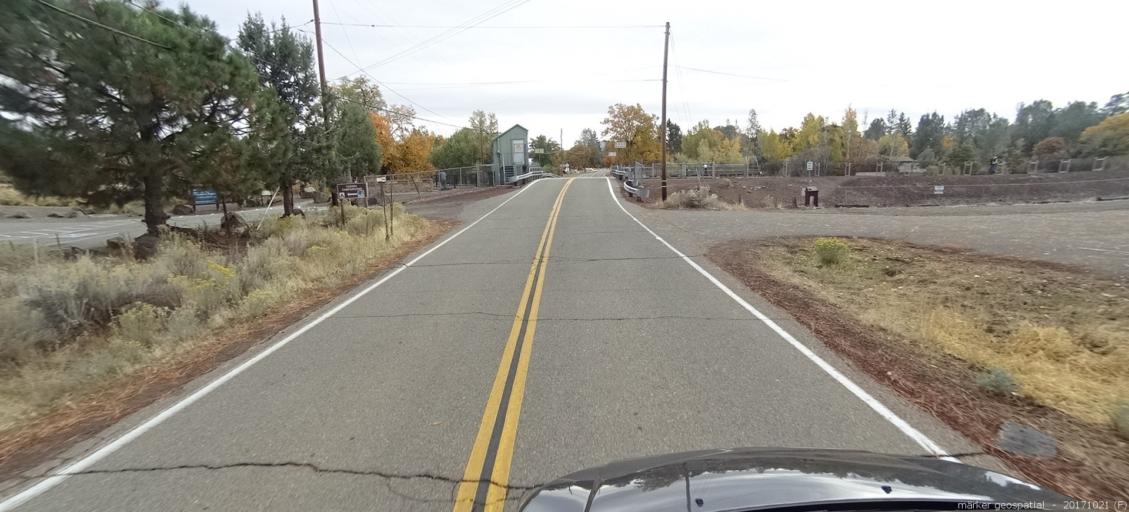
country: US
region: California
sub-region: Shasta County
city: Burney
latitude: 40.9193
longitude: -121.5527
